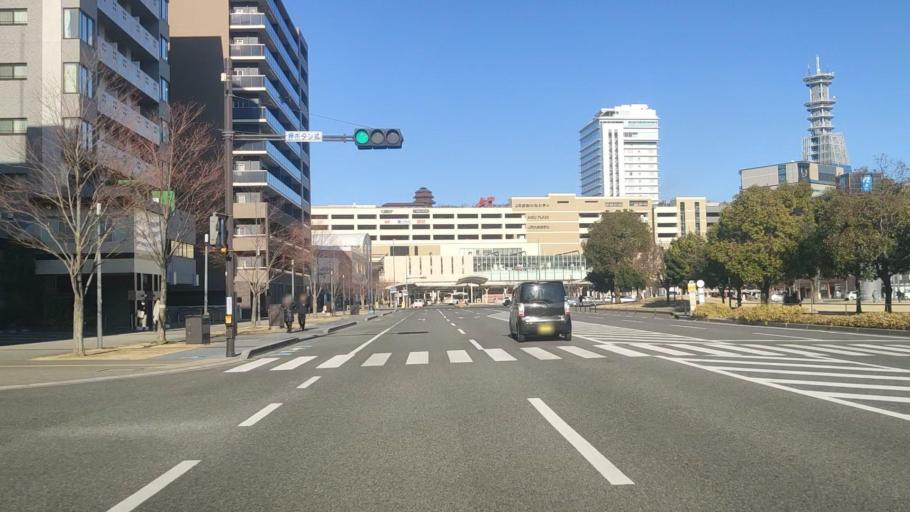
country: JP
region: Oita
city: Oita
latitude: 33.2308
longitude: 131.6041
